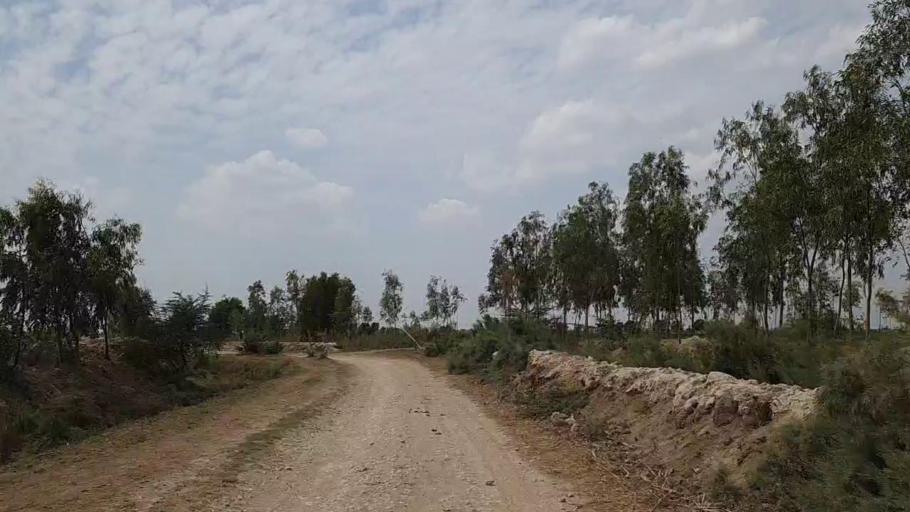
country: PK
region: Sindh
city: Daro Mehar
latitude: 24.7836
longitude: 68.2035
